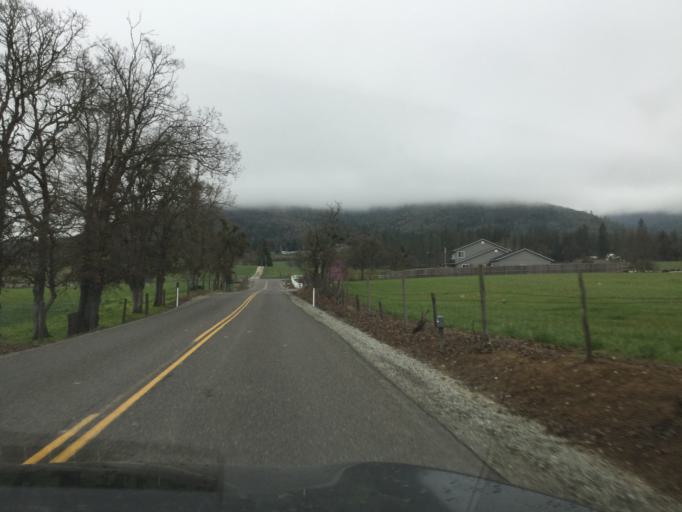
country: US
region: Oregon
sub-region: Jackson County
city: Central Point
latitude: 42.3921
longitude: -122.9686
